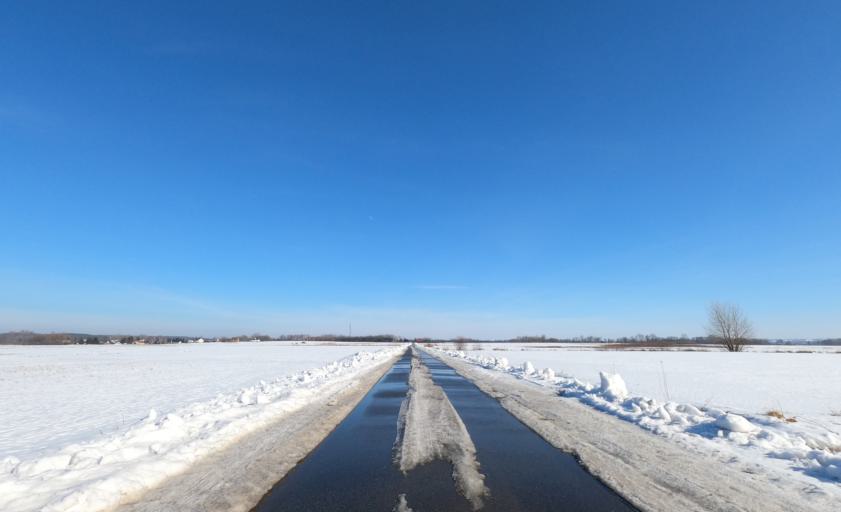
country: PL
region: Subcarpathian Voivodeship
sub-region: Powiat debicki
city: Brzeznica
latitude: 50.0833
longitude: 21.4995
